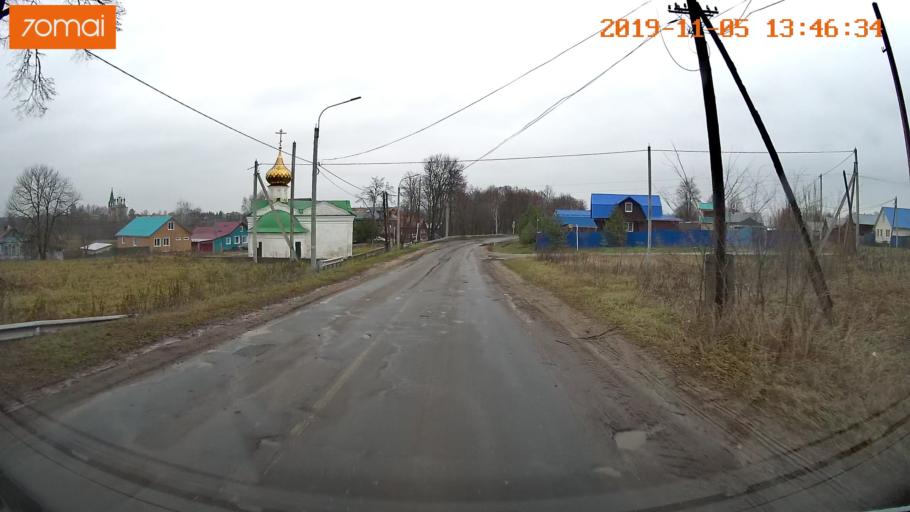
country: RU
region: Ivanovo
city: Shuya
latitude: 56.9960
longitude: 41.4099
